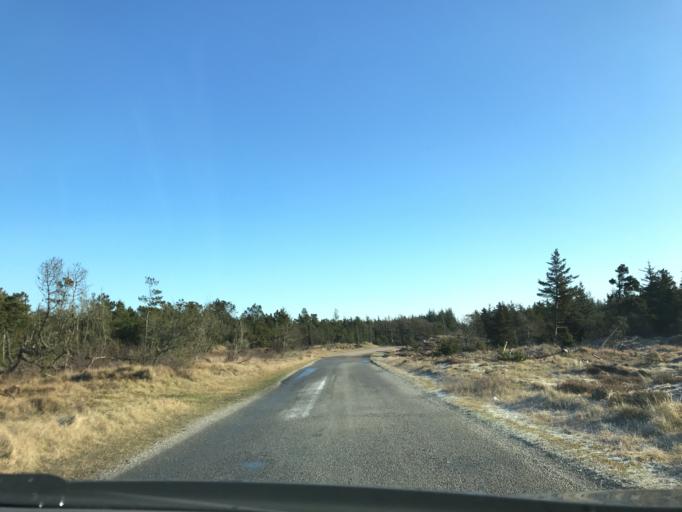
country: DK
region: South Denmark
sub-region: Varde Kommune
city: Oksbol
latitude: 55.7918
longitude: 8.1928
